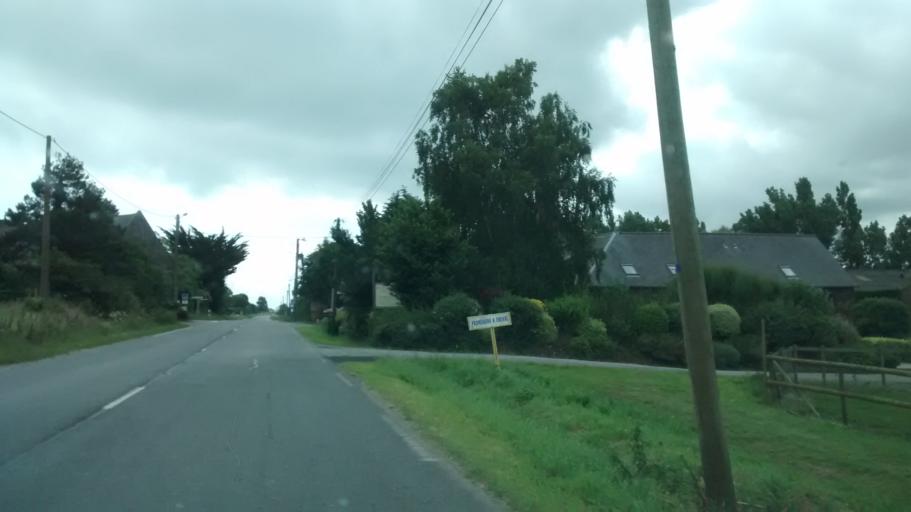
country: FR
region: Brittany
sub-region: Departement d'Ille-et-Vilaine
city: Saint-Meloir-des-Ondes
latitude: 48.6415
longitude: -1.8762
